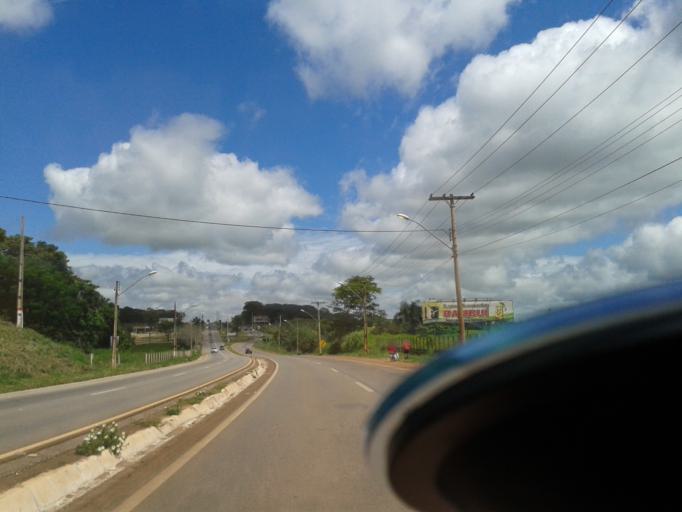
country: BR
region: Goias
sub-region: Goianira
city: Goianira
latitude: -16.4954
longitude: -49.4217
